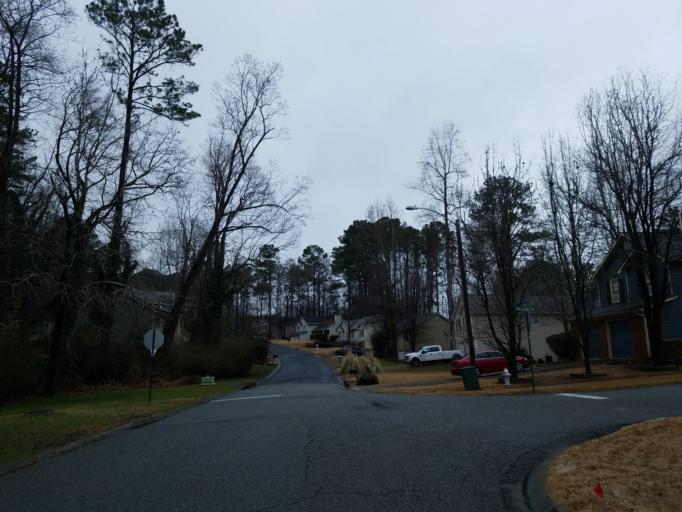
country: US
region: Georgia
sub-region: Cobb County
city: Acworth
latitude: 34.0734
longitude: -84.6631
